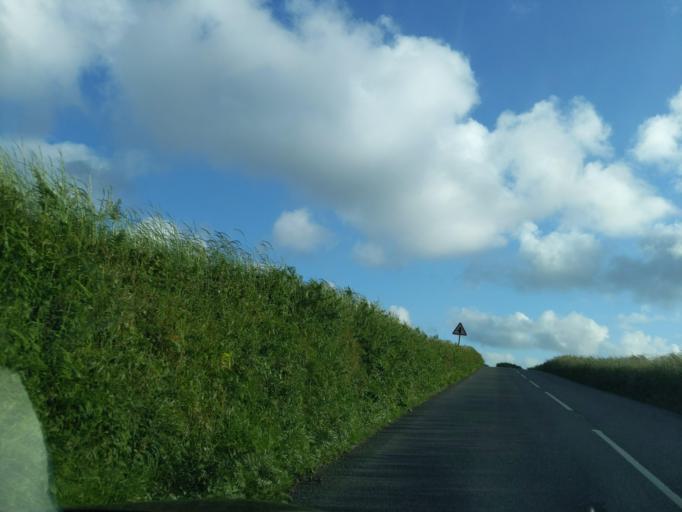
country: GB
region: England
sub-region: Devon
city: Fremington
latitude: 51.0155
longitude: -4.1043
